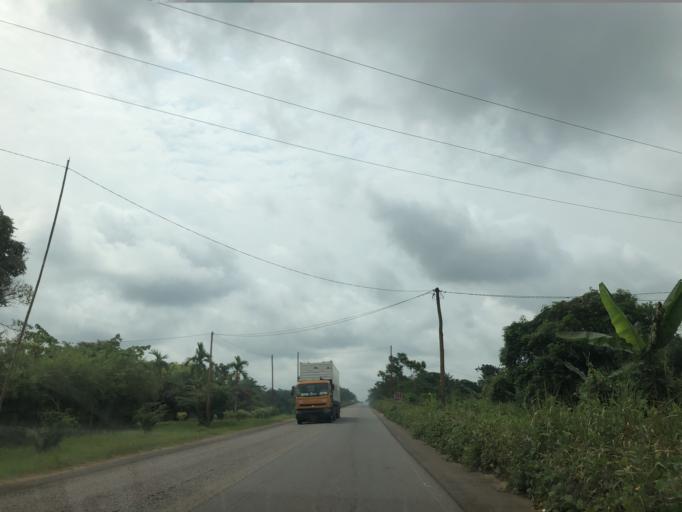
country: CM
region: Littoral
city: Edea
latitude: 3.7628
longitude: 10.1250
